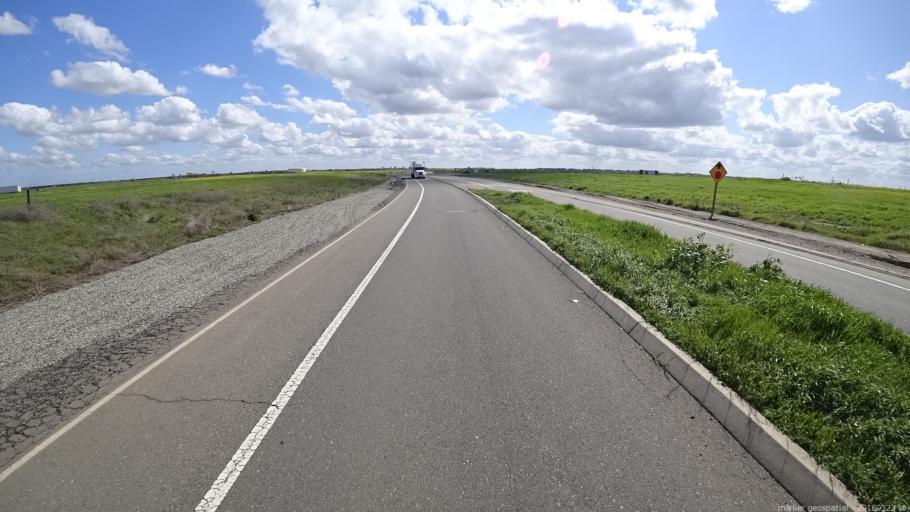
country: US
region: California
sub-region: Yolo County
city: West Sacramento
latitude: 38.6829
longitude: -121.5691
